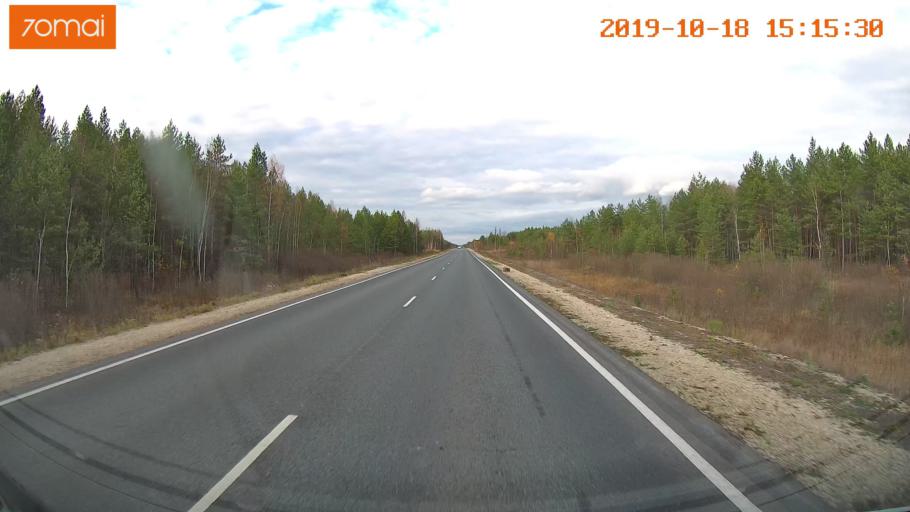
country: RU
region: Vladimir
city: Gus'-Khrustal'nyy
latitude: 55.6199
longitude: 40.7226
